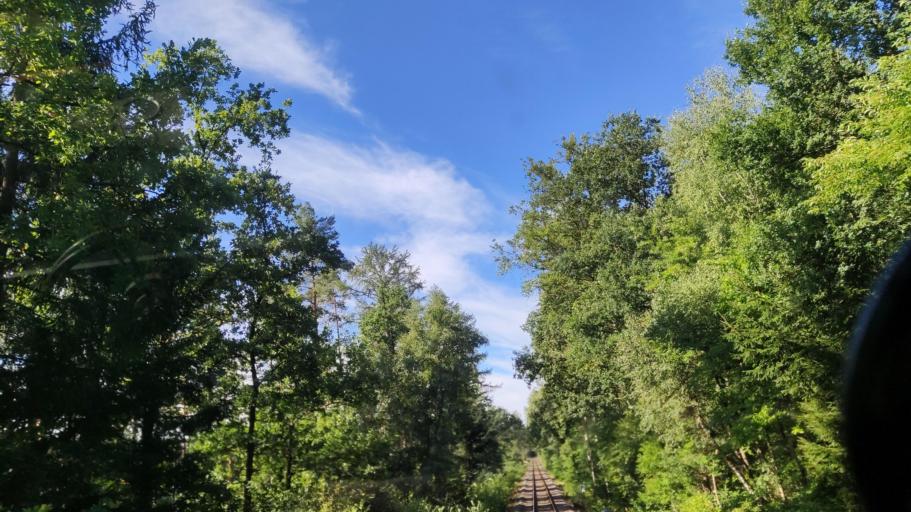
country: DE
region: Lower Saxony
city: Bispingen
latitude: 53.0730
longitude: 9.9870
